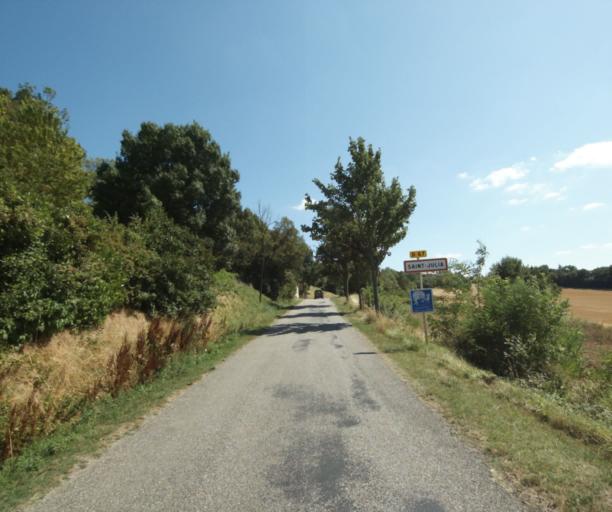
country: FR
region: Midi-Pyrenees
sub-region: Departement de la Haute-Garonne
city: Saint-Felix-Lauragais
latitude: 43.4931
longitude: 1.8972
